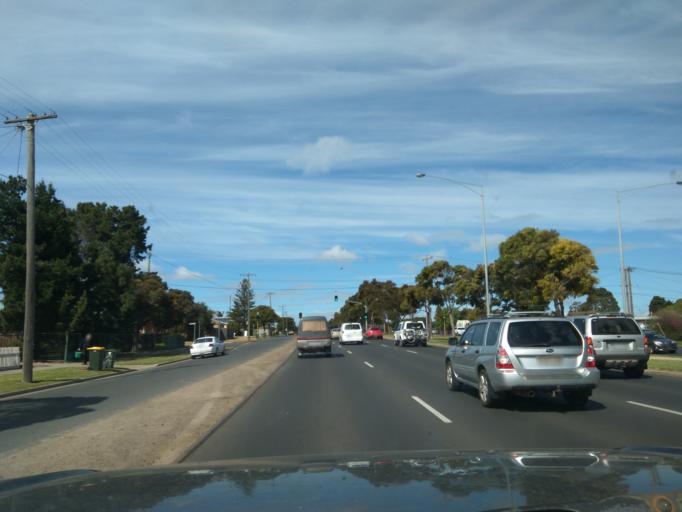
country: AU
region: Victoria
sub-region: Greater Geelong
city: Bell Park
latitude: -38.0861
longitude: 144.3578
